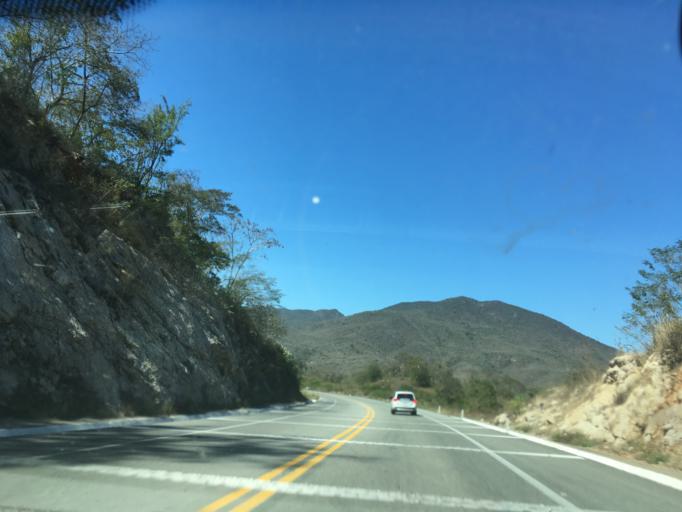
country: MX
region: Michoacan
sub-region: Arteaga
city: Infiernillo (Morelos de Infiernillo)
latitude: 18.1719
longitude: -101.9053
